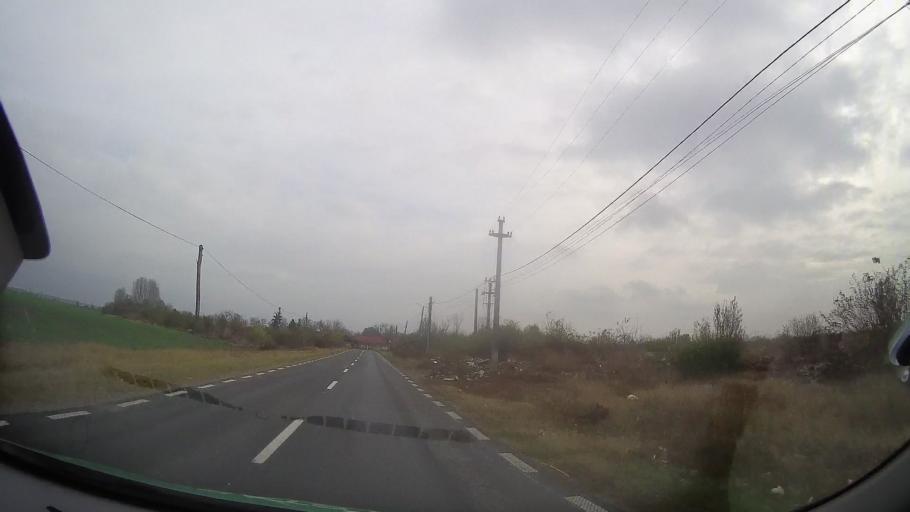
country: RO
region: Ilfov
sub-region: Comuna Gruiu
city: Lipia
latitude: 44.7181
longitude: 26.2722
